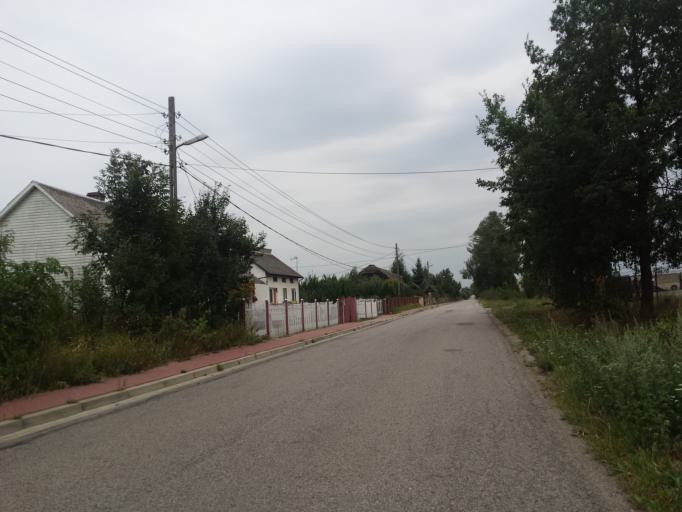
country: PL
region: Swietokrzyskie
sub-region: Powiat kielecki
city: Morawica
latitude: 50.7345
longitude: 20.6707
